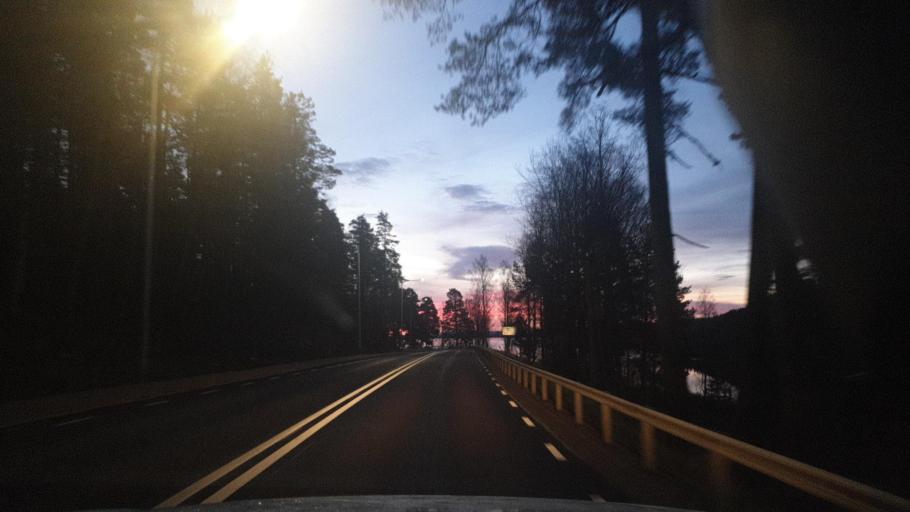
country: SE
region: Vaermland
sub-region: Arvika Kommun
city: Arvika
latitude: 59.6711
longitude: 12.4750
